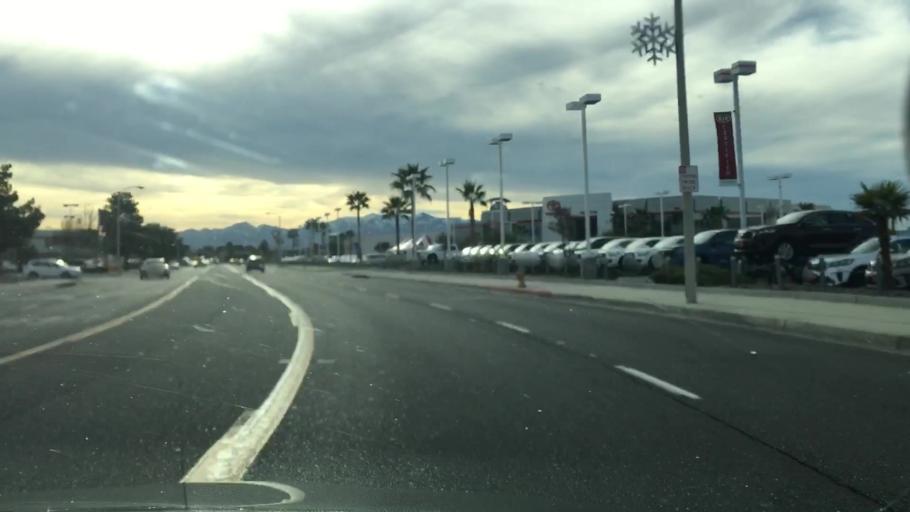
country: US
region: California
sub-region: San Bernardino County
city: Victorville
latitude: 34.5179
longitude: -117.3173
